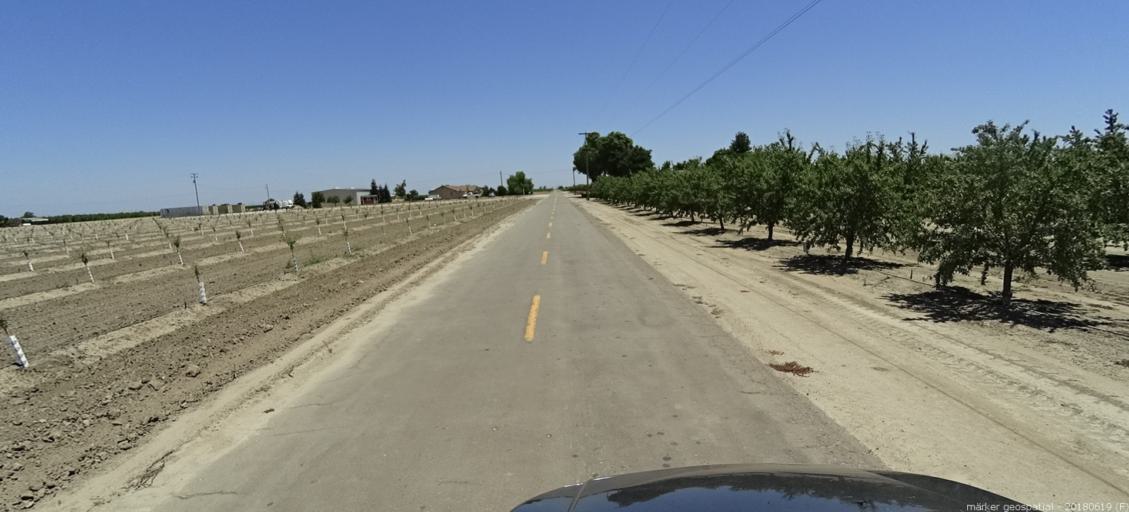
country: US
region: California
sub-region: Madera County
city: Parkwood
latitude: 36.8585
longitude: -120.1029
